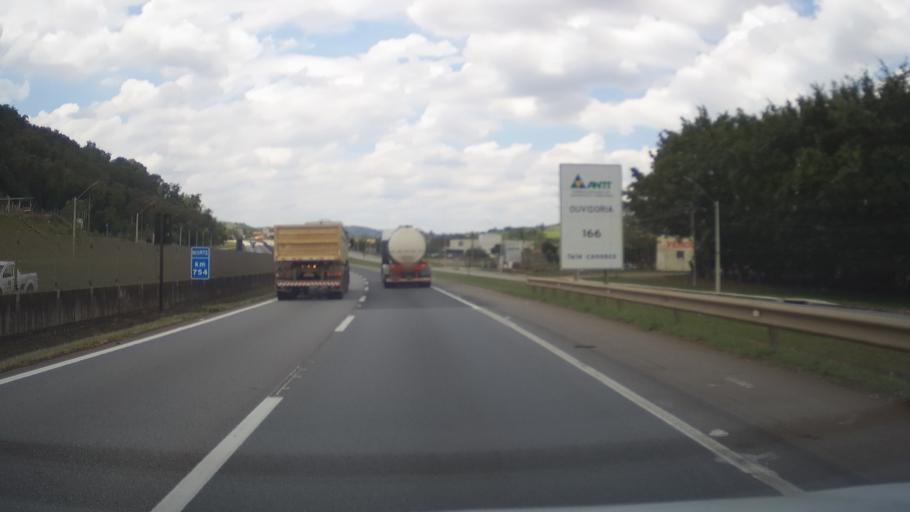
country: BR
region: Minas Gerais
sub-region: Tres Coracoes
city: Tres Coracoes
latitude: -21.6671
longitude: -45.3155
